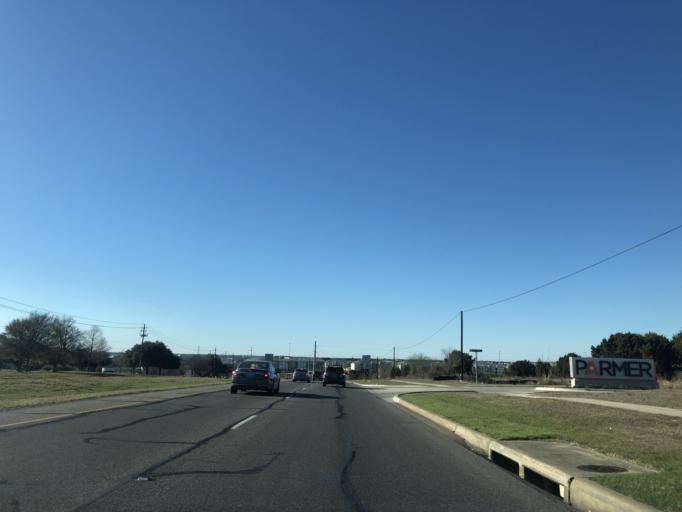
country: US
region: Texas
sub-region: Travis County
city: Wells Branch
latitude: 30.4040
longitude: -97.6600
